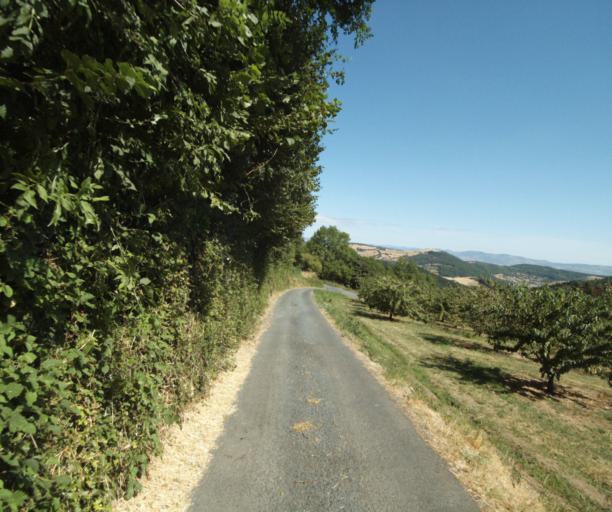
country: FR
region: Rhone-Alpes
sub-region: Departement du Rhone
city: Montrottier
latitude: 45.8073
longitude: 4.4952
